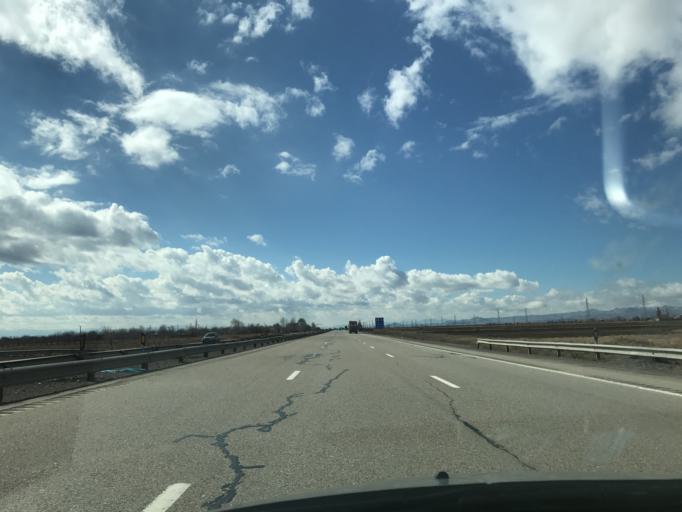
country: IR
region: Qazvin
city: Qazvin
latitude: 36.2381
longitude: 49.9076
